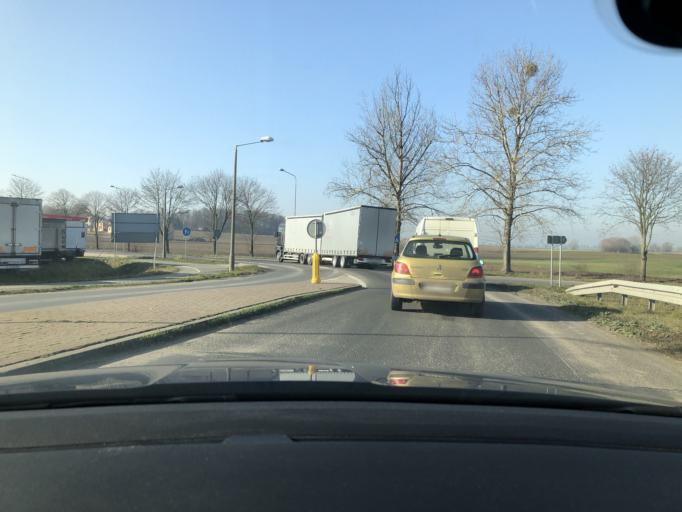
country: PL
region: Greater Poland Voivodeship
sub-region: Powiat poznanski
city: Buk
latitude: 52.3655
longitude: 16.5362
